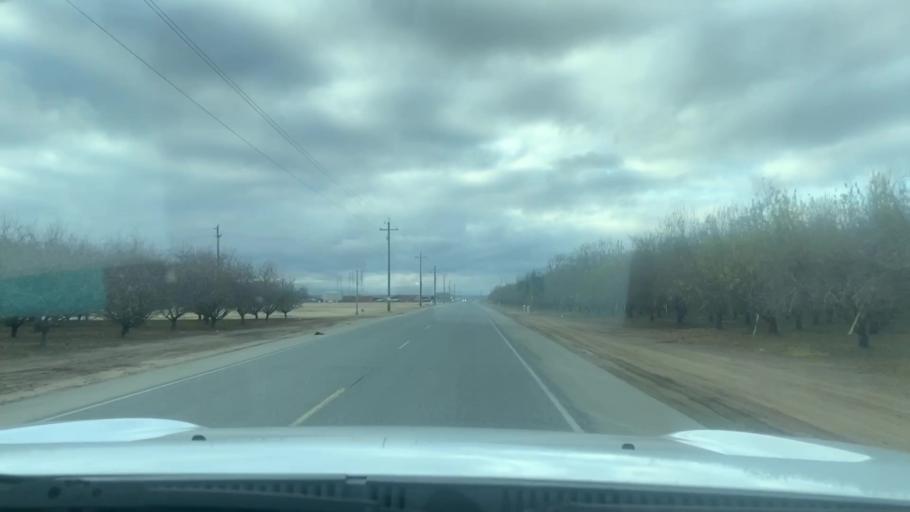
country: US
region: California
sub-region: Kern County
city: Buttonwillow
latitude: 35.5007
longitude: -119.5185
